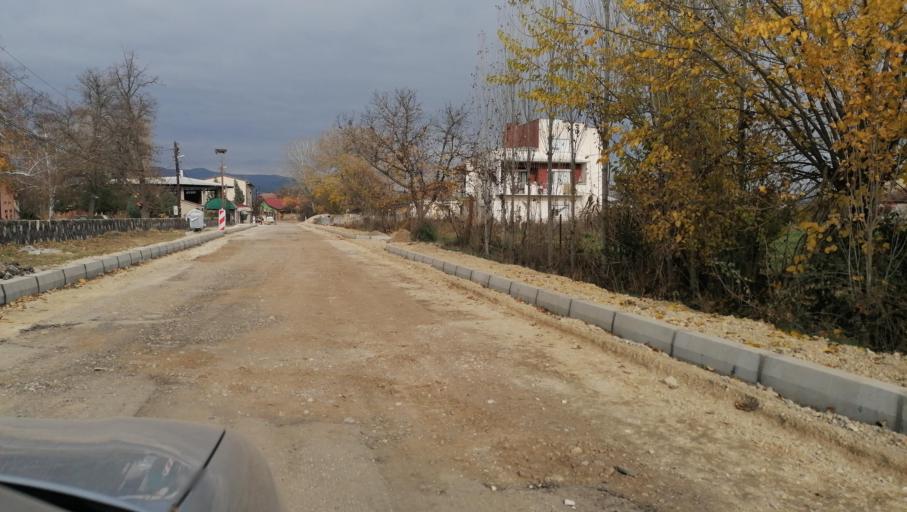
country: MK
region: Cesinovo-Oblesevo
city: Cesinovo
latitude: 41.8740
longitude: 22.2938
